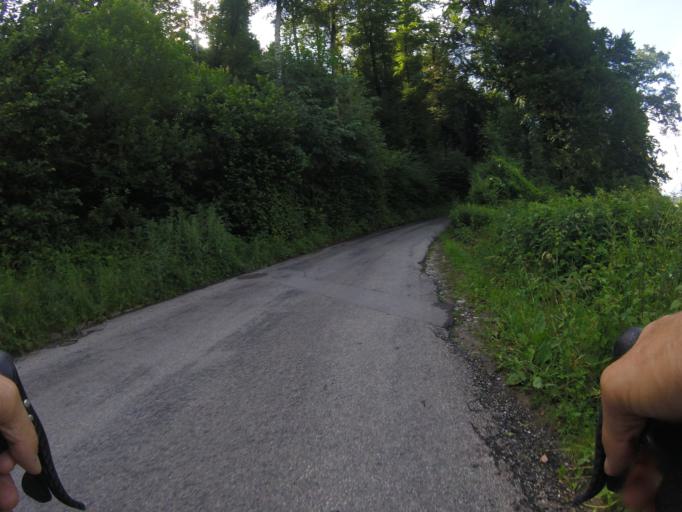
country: CH
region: Bern
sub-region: Bern-Mittelland District
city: Stettlen
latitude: 46.9405
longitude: 7.5095
